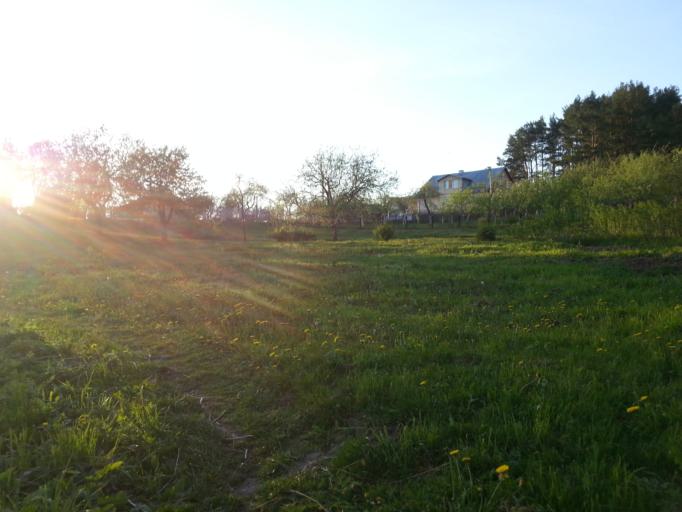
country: BY
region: Minsk
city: Slabada
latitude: 54.0498
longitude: 27.8689
